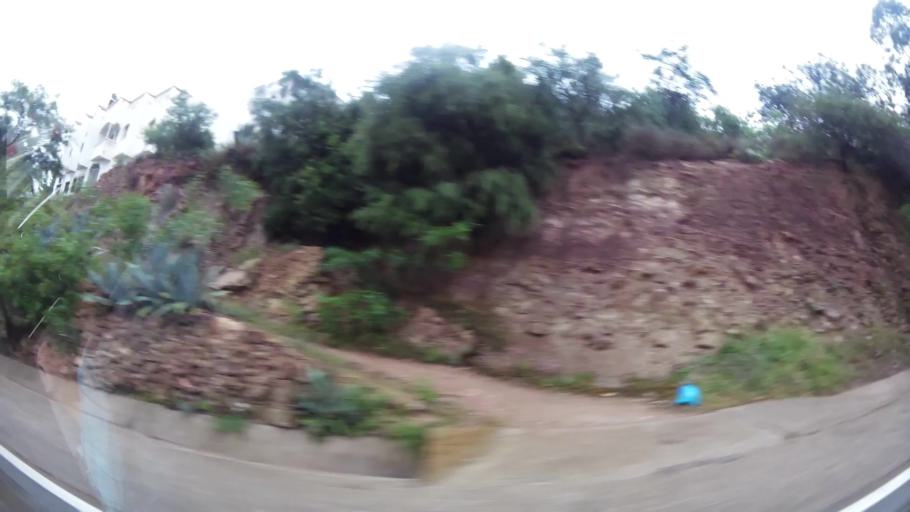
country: MA
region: Taza-Al Hoceima-Taounate
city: Tirhanimine
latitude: 35.2262
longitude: -3.9301
